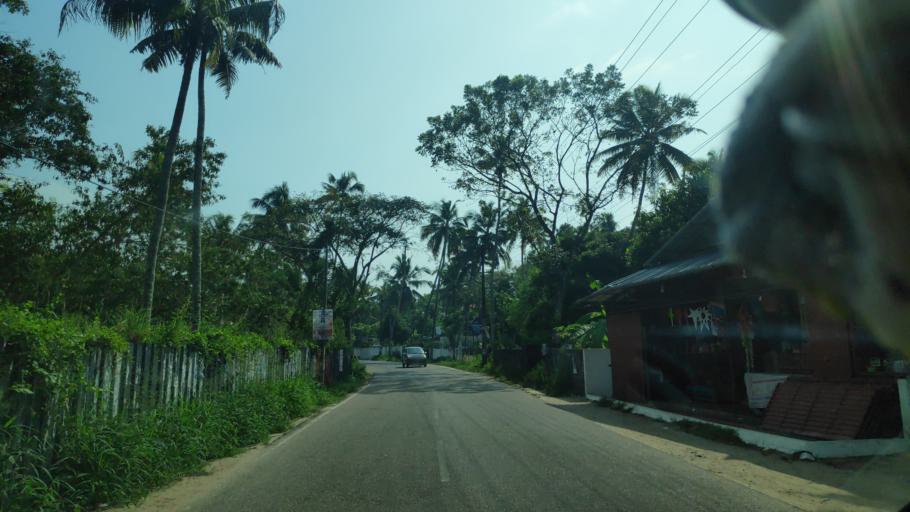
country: IN
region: Kerala
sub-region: Alappuzha
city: Shertallai
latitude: 9.6194
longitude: 76.3005
